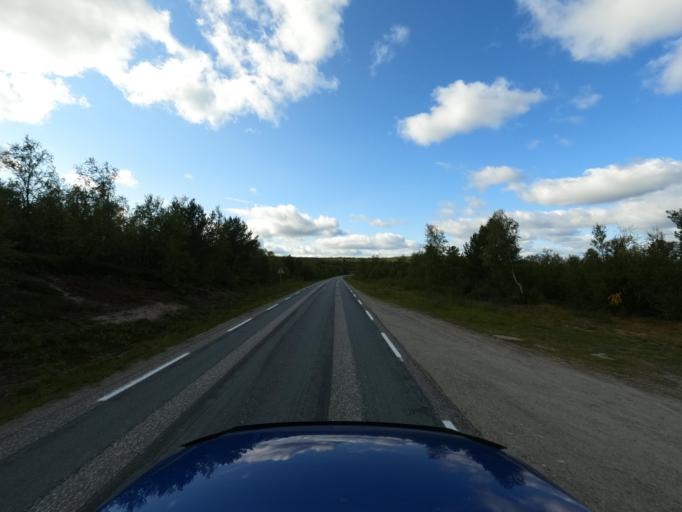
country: NO
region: Finnmark Fylke
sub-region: Karasjok
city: Karasjohka
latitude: 69.4297
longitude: 25.7835
